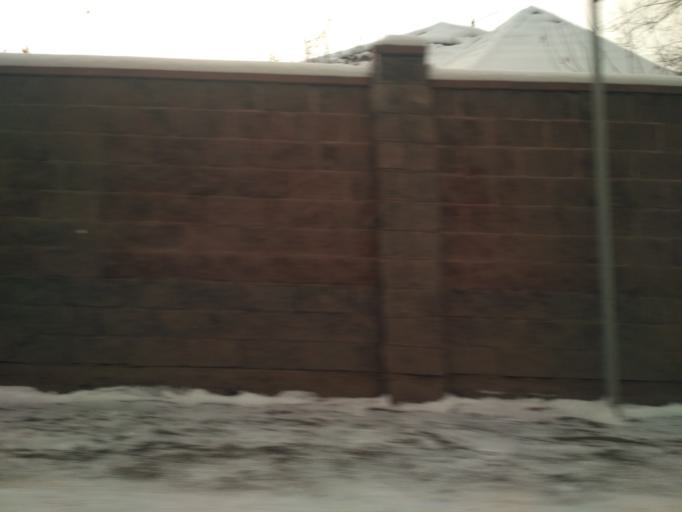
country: KZ
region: Almaty Qalasy
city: Almaty
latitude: 43.2169
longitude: 76.7658
